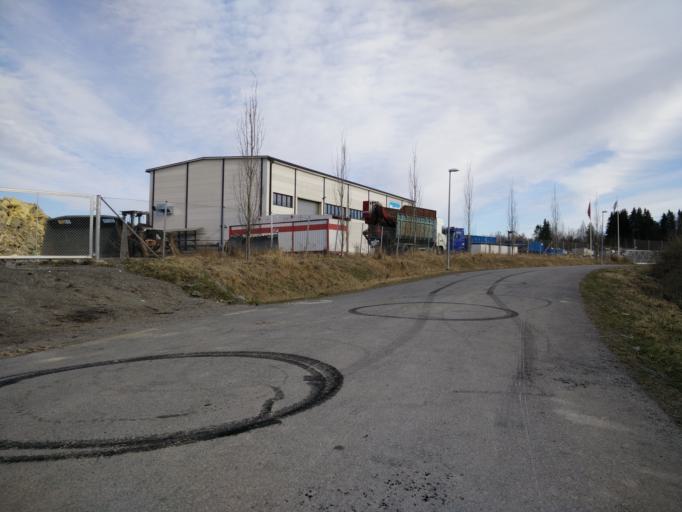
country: FI
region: Pirkanmaa
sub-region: Tampere
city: Orivesi
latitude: 61.6975
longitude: 24.3516
